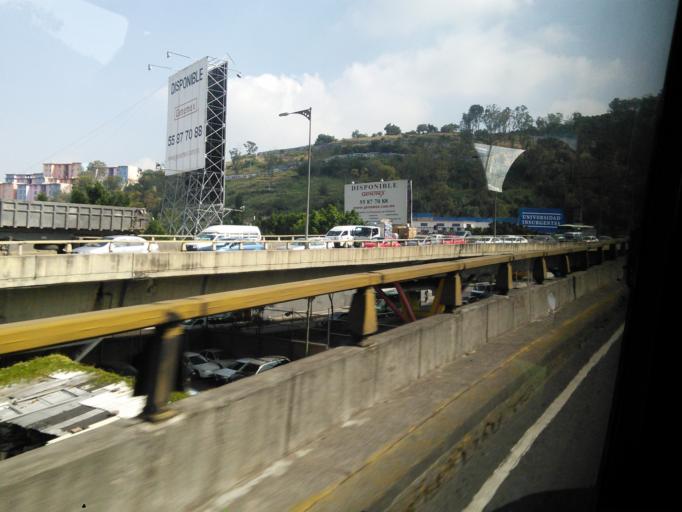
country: MX
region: Mexico
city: Colonia Lindavista
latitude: 19.5006
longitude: -99.1180
